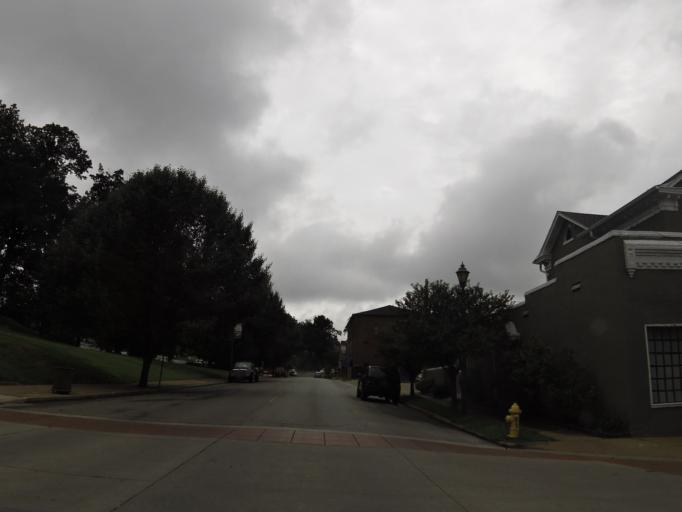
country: US
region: Missouri
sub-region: Cape Girardeau County
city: Cape Girardeau
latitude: 37.3049
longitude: -89.5194
